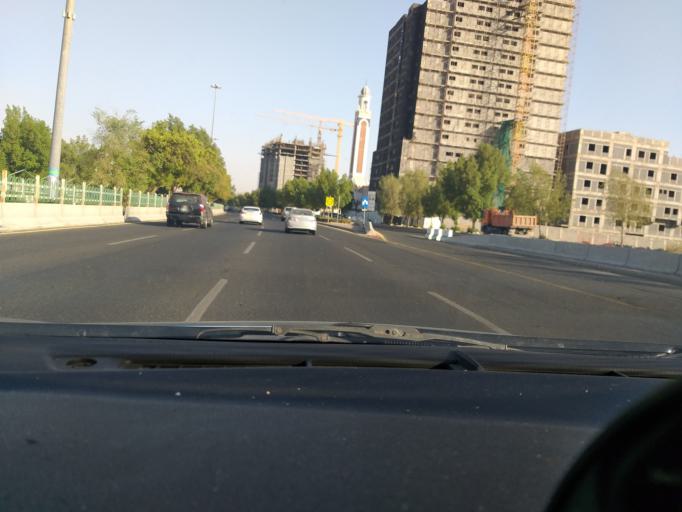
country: SA
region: Makkah
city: Mecca
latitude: 21.3762
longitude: 39.8779
